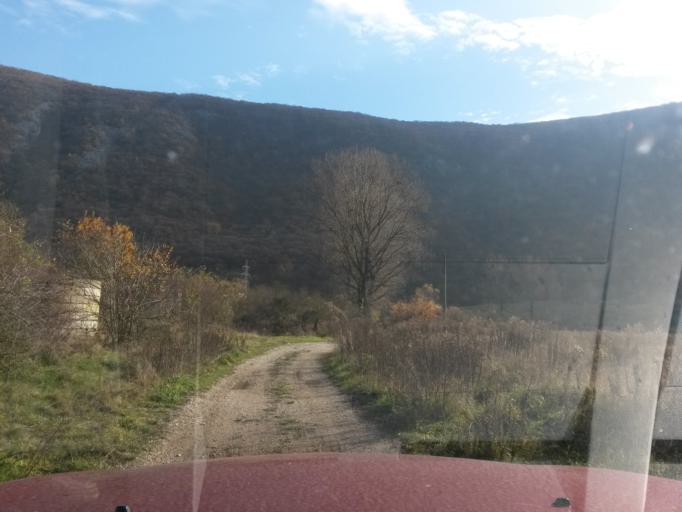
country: SK
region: Kosicky
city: Roznava
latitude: 48.5898
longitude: 20.4771
